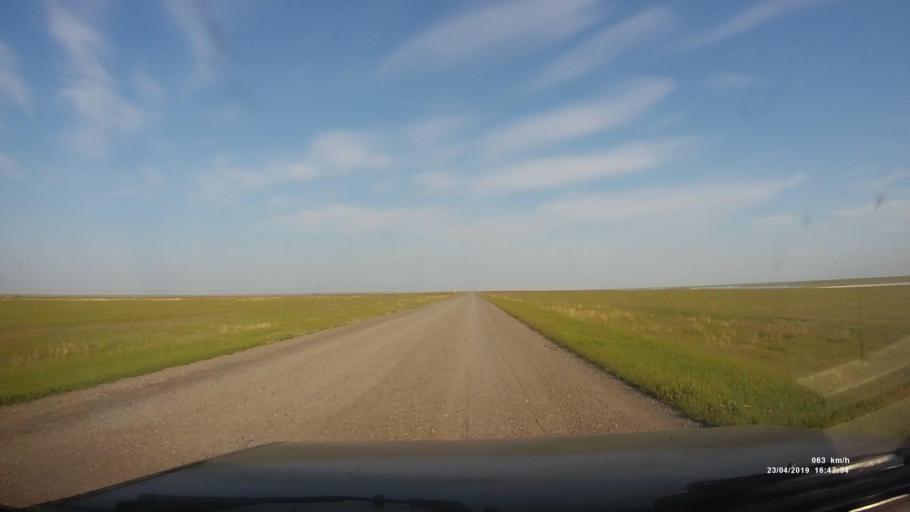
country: RU
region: Kalmykiya
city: Priyutnoye
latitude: 46.3382
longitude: 43.2496
